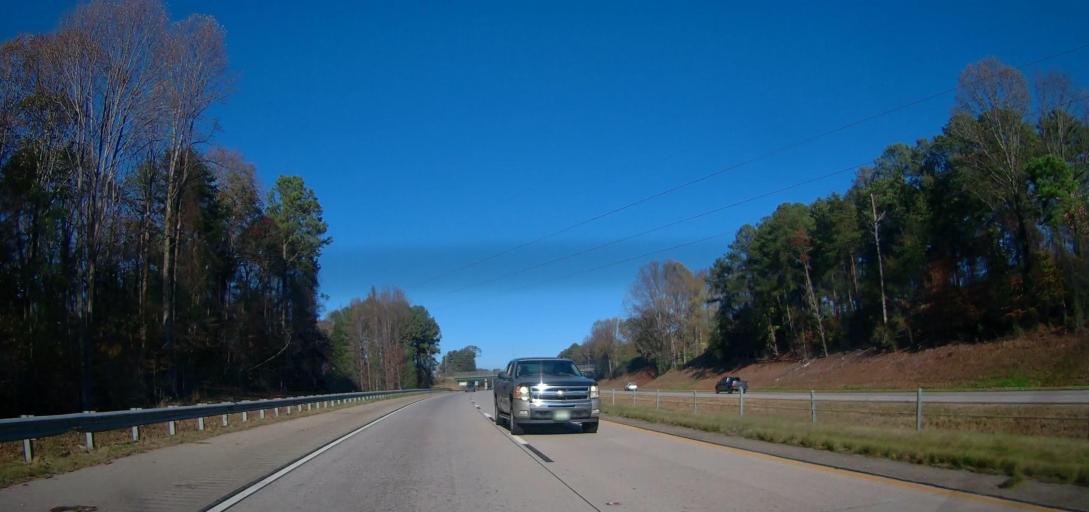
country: US
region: Georgia
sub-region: Hall County
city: Gainesville
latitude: 34.2871
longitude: -83.8050
